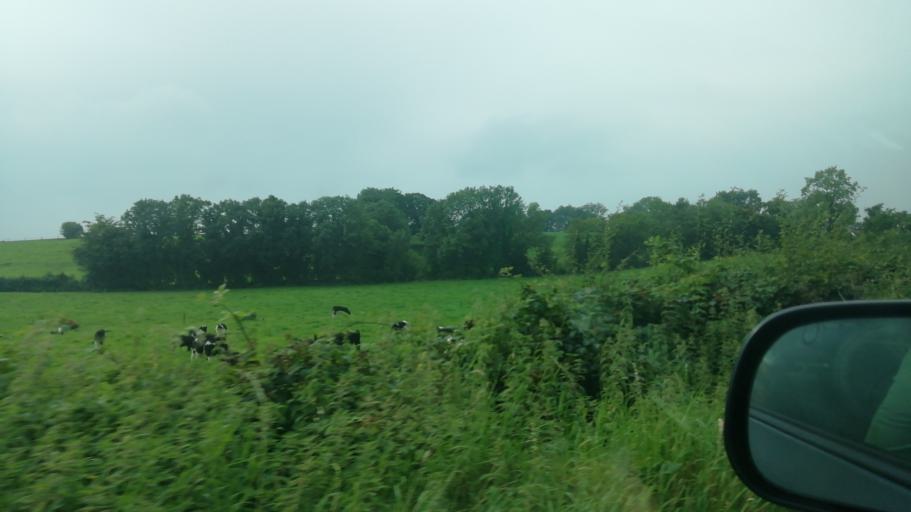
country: IE
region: Munster
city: Fethard
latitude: 52.5782
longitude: -7.6419
